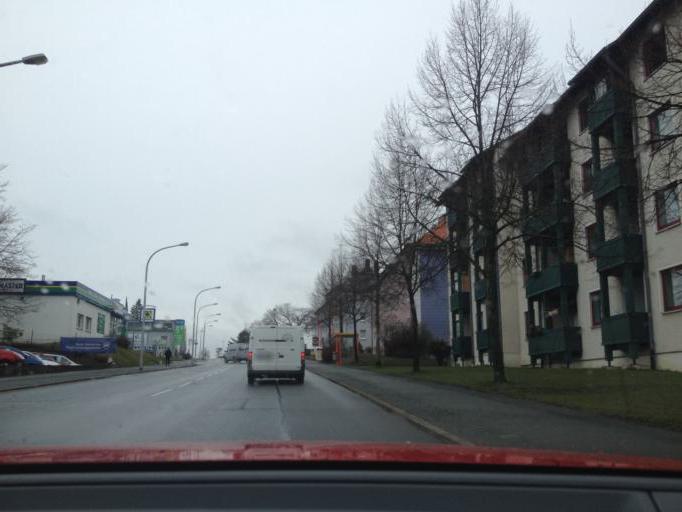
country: DE
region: Bavaria
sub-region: Upper Franconia
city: Hof
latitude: 50.3025
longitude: 11.9249
